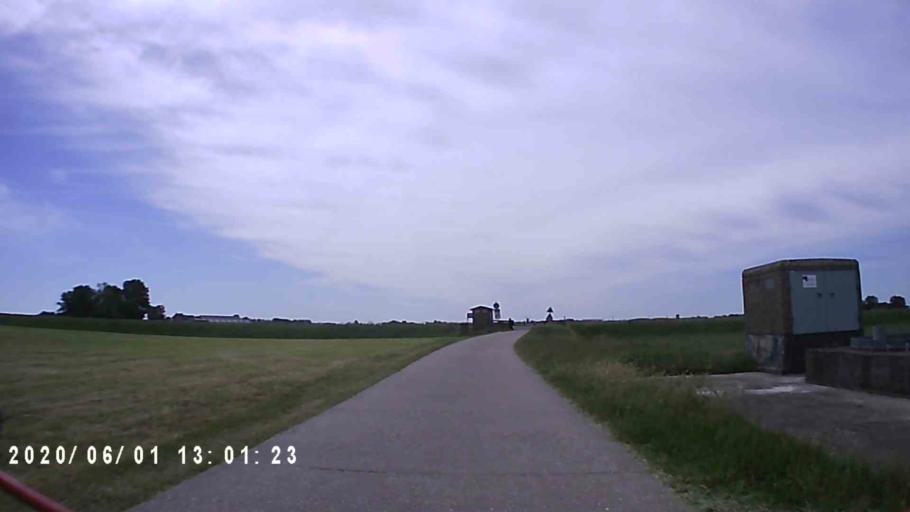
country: NL
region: Friesland
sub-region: Gemeente Franekeradeel
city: Tzum
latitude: 53.1448
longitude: 5.5382
